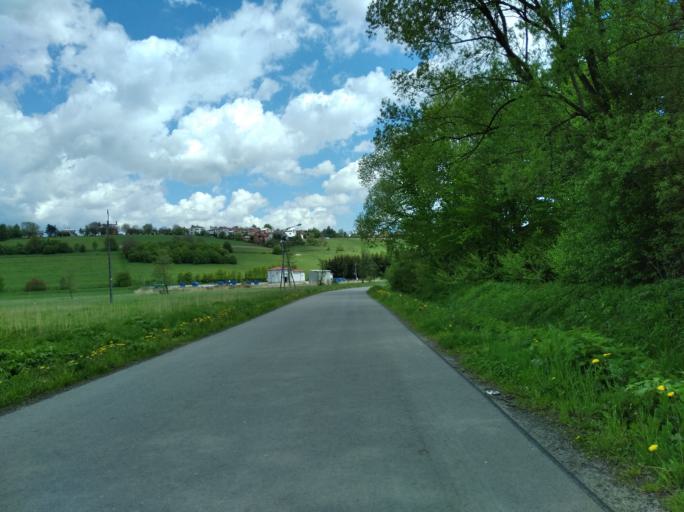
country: PL
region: Subcarpathian Voivodeship
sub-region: Powiat strzyzowski
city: Frysztak
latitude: 49.8320
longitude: 21.5961
